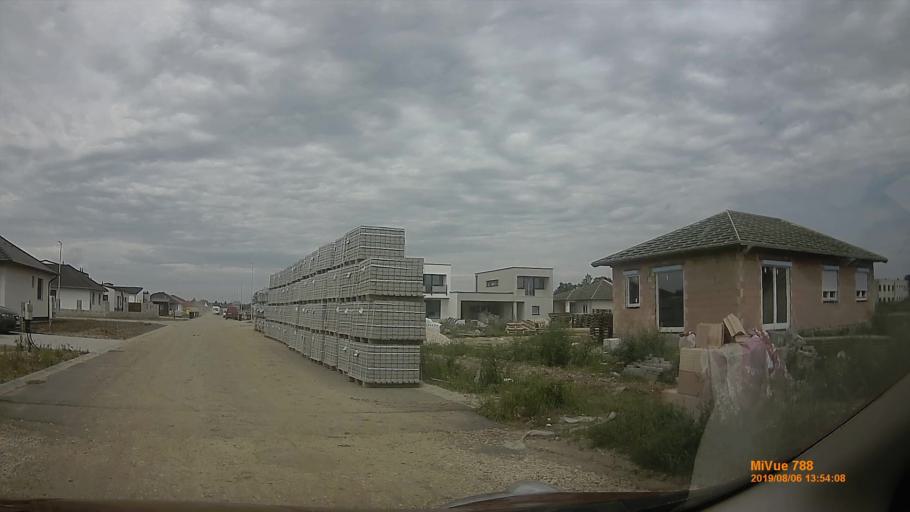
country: HU
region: Vas
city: Szombathely
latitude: 47.2488
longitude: 16.6007
